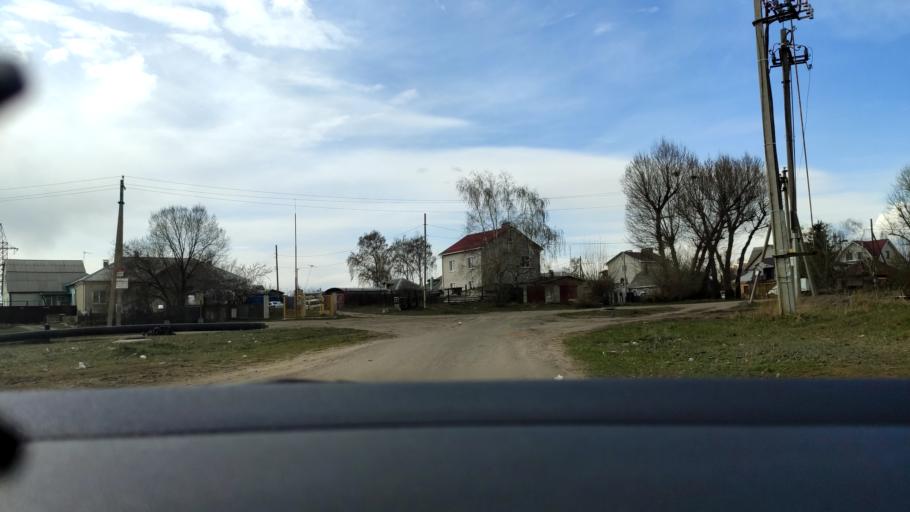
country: RU
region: Voronezj
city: Maslovka
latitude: 51.6282
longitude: 39.2781
